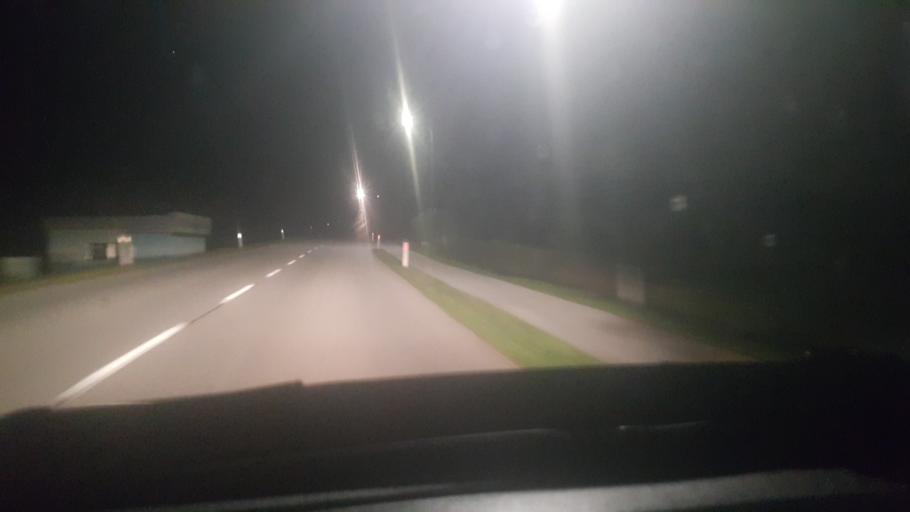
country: AT
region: Carinthia
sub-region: Politischer Bezirk Feldkirchen
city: Feldkirchen in Karnten
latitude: 46.7144
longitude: 14.1022
